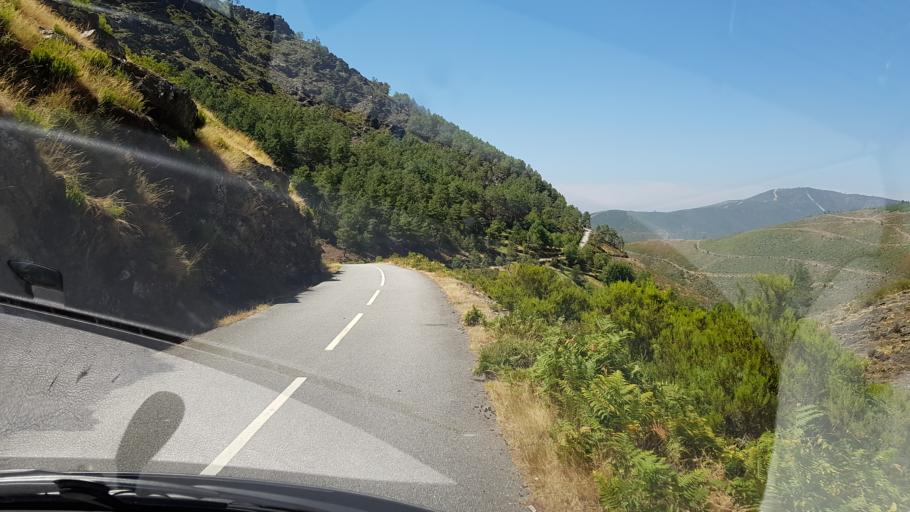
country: PT
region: Vila Real
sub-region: Mondim de Basto
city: Mondim de Basto
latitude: 41.3300
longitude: -7.8848
